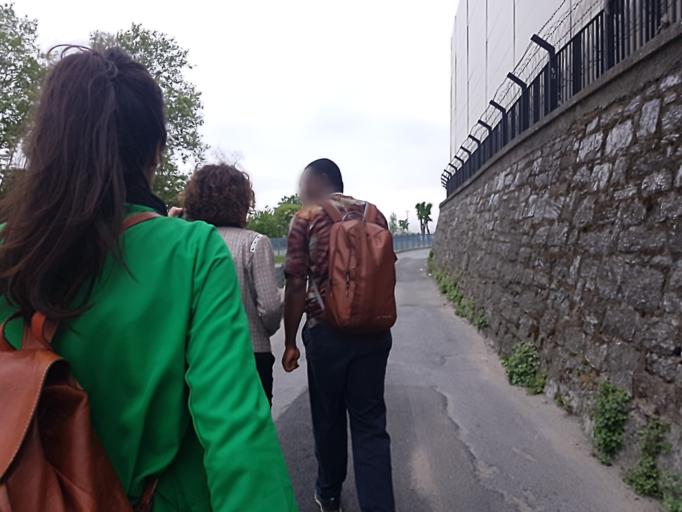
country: TR
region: Istanbul
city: Sisli
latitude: 41.0450
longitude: 28.9900
